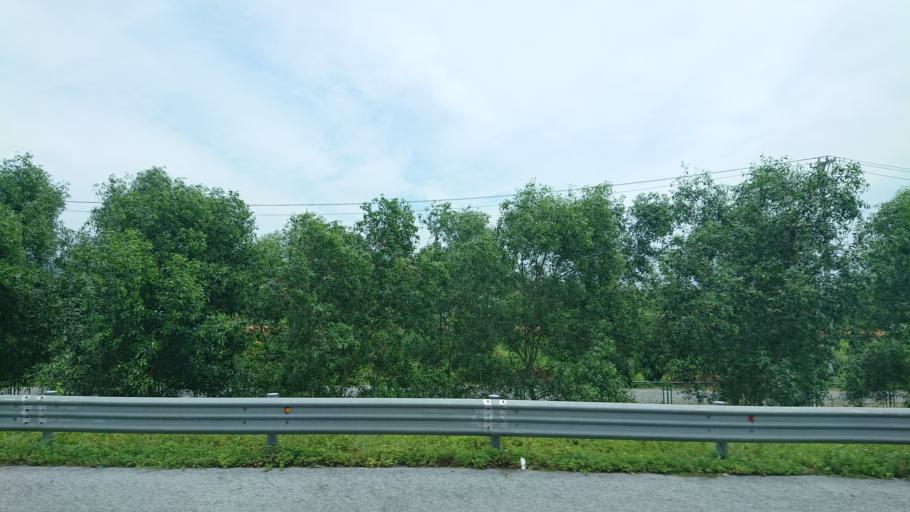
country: VN
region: Hai Phong
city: Nui Doi
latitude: 20.7698
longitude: 106.6265
